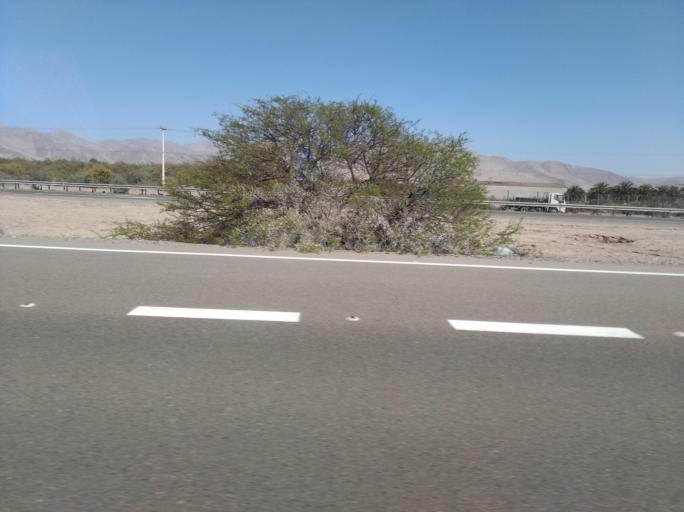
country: CL
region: Atacama
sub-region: Provincia de Copiapo
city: Copiapo
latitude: -27.3311
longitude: -70.5723
